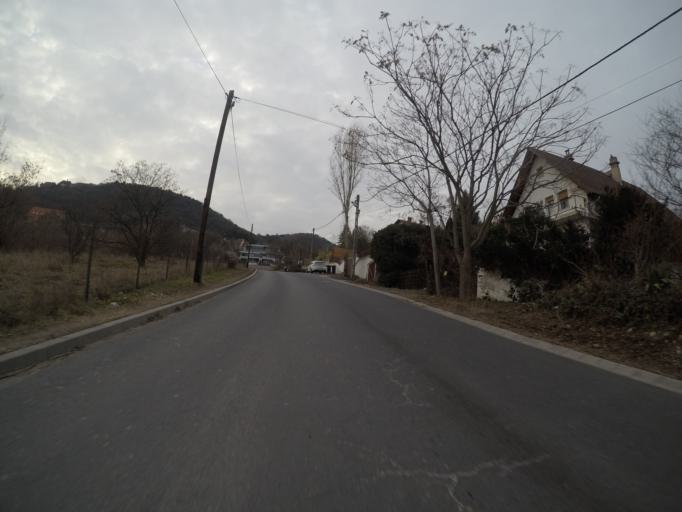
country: HU
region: Budapest
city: Budapest III. keruelet
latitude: 47.5435
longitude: 19.0216
